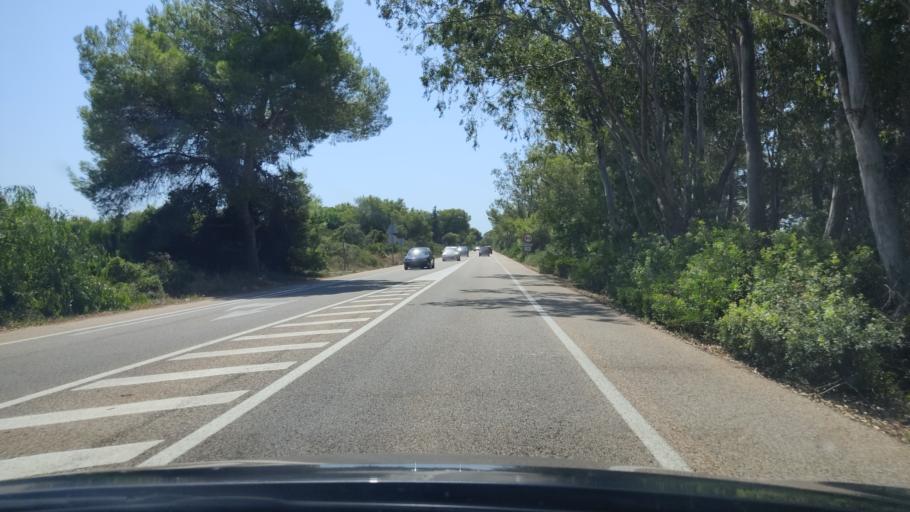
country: ES
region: Valencia
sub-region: Provincia de Valencia
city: Sollana
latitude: 39.3193
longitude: -0.3070
